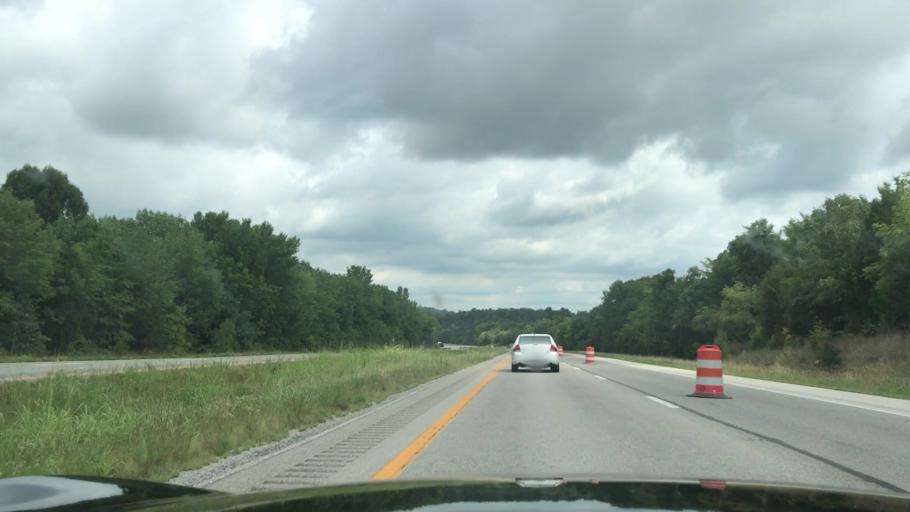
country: US
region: Kentucky
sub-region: Butler County
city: Morgantown
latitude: 37.1153
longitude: -86.6413
